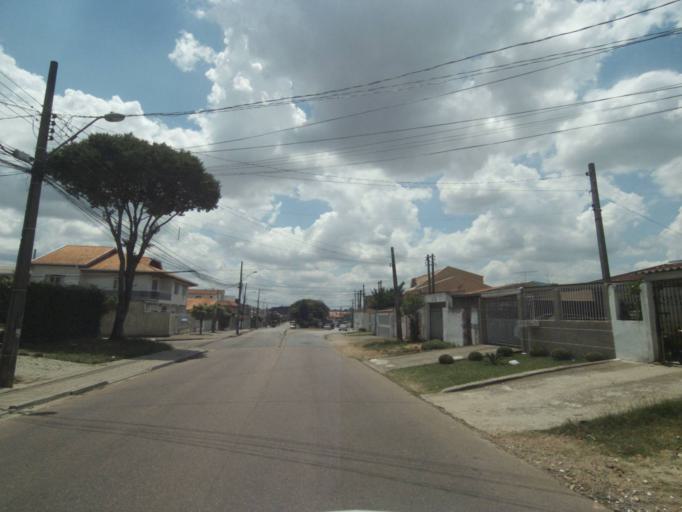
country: BR
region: Parana
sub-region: Sao Jose Dos Pinhais
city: Sao Jose dos Pinhais
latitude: -25.5414
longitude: -49.2641
